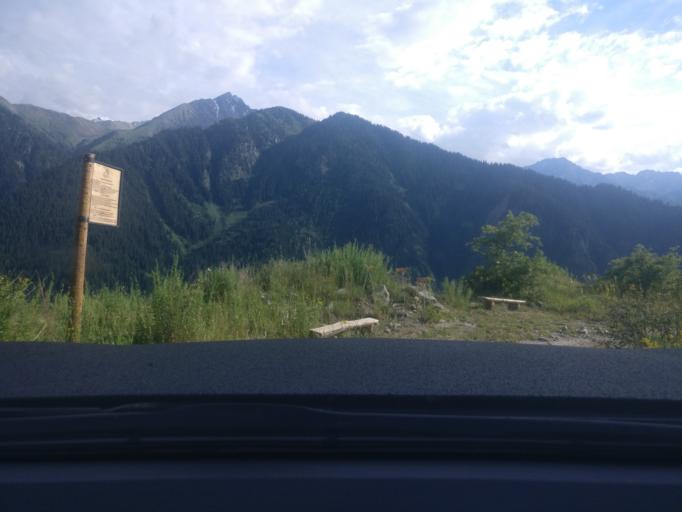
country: KZ
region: Almaty Qalasy
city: Almaty
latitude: 43.1076
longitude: 76.9386
